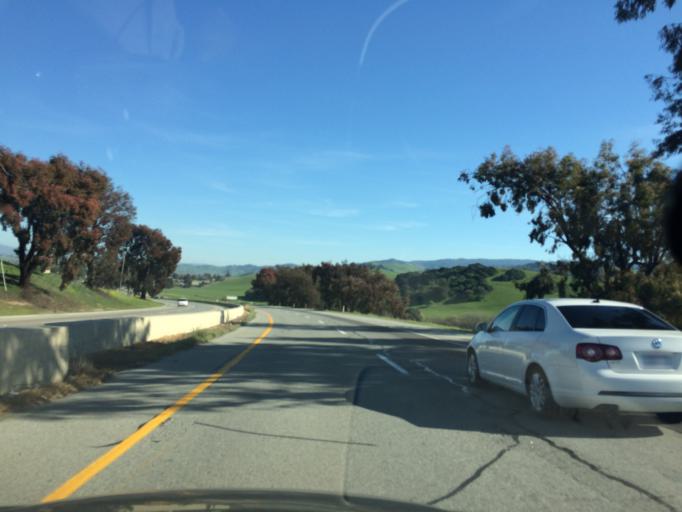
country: US
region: California
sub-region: San Benito County
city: San Juan Bautista
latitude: 36.8493
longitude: -121.5603
